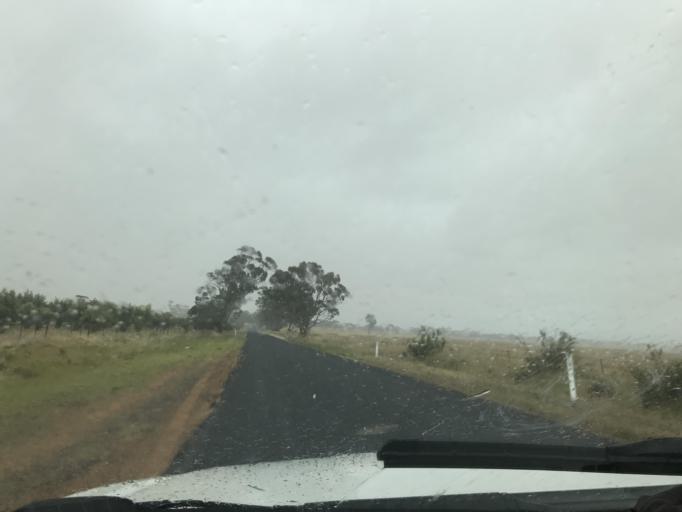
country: AU
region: South Australia
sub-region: Tatiara
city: Bordertown
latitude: -36.3296
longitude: 141.2127
